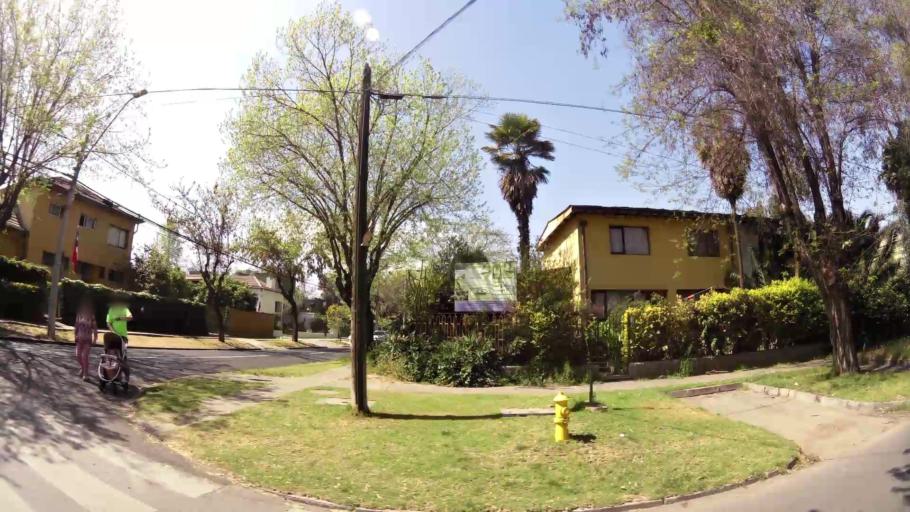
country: CL
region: Santiago Metropolitan
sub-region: Provincia de Santiago
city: Villa Presidente Frei, Nunoa, Santiago, Chile
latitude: -33.4435
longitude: -70.5617
